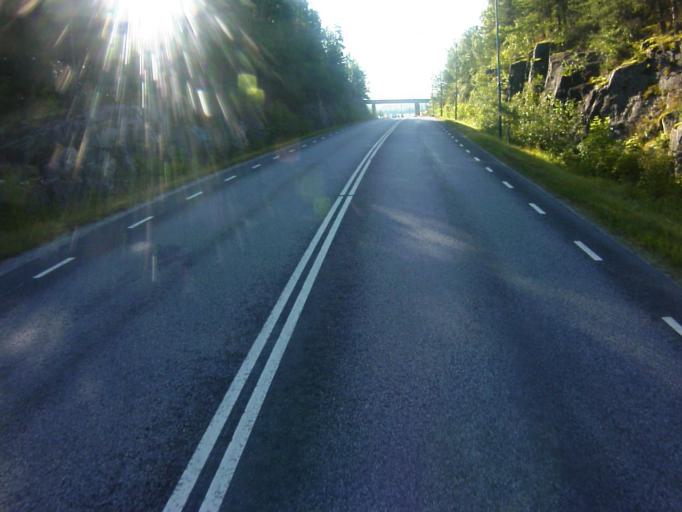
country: SE
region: Soedermanland
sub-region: Eskilstuna Kommun
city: Hallbybrunn
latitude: 59.3969
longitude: 16.4379
